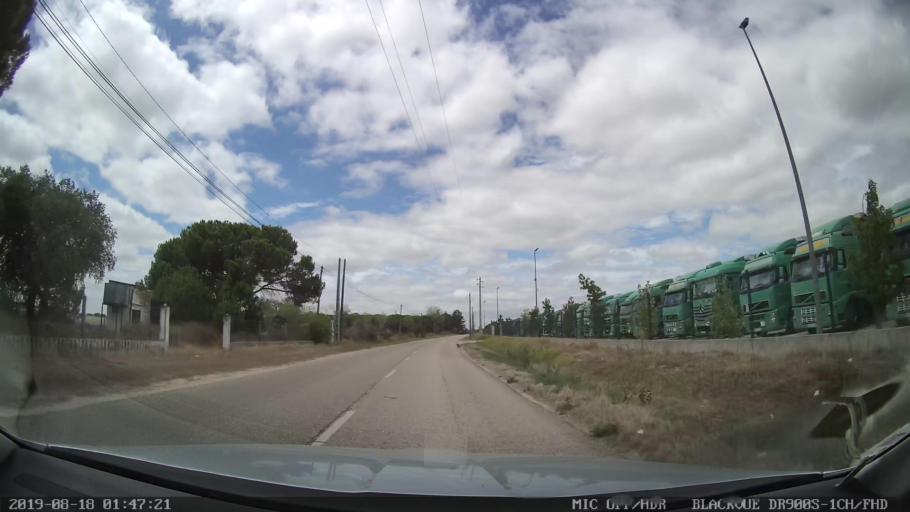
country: PT
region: Santarem
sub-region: Benavente
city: Benavente
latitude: 38.9382
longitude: -8.7919
